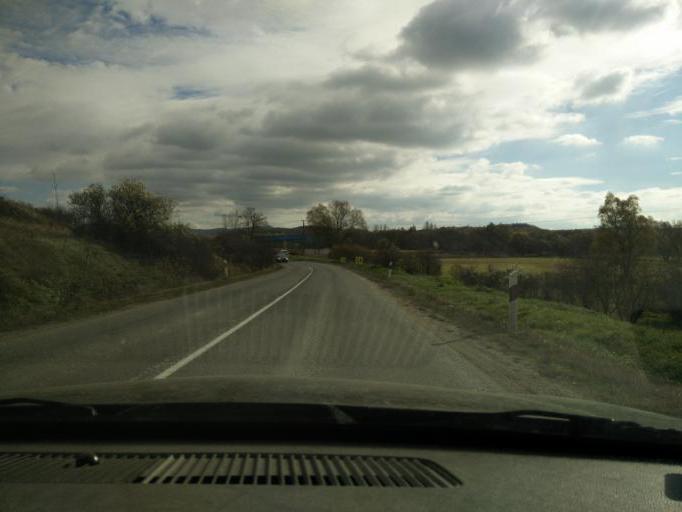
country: HU
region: Komarom-Esztergom
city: Piliscsev
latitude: 47.6594
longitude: 18.7830
